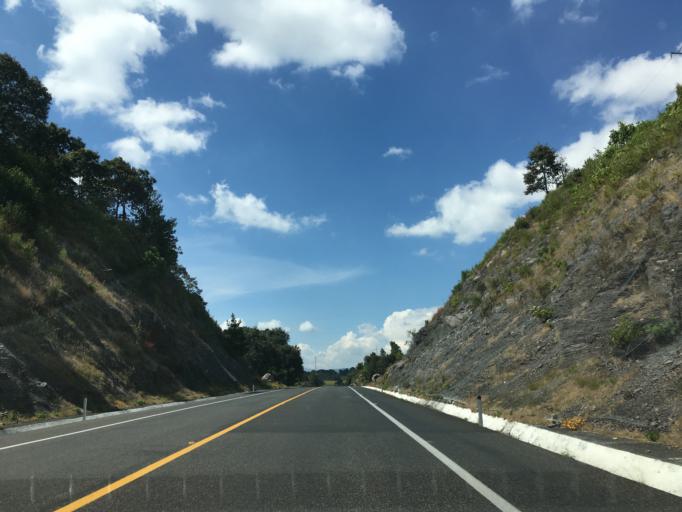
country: MX
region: Michoacan
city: Patzcuaro
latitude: 19.4986
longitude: -101.6305
